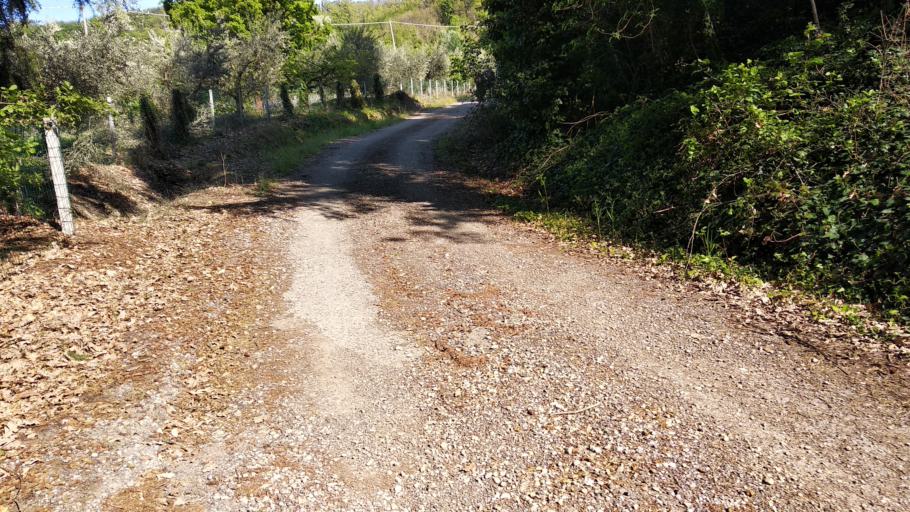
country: IT
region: Emilia-Romagna
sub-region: Provincia di Ravenna
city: Fognano
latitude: 44.2304
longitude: 11.7199
